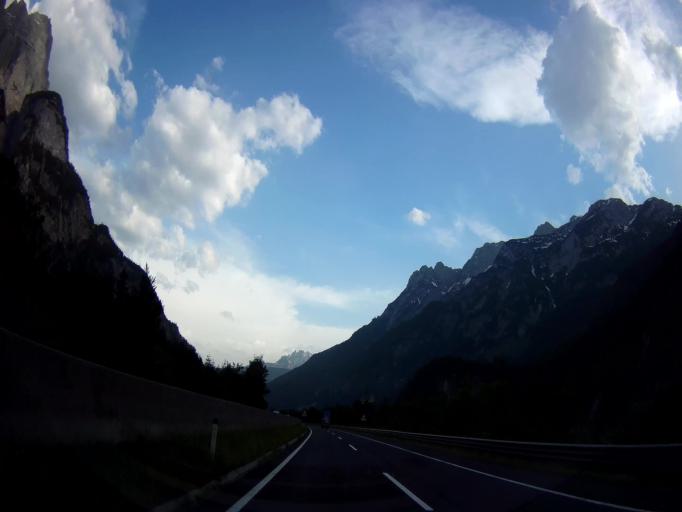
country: AT
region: Salzburg
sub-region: Politischer Bezirk Hallein
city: Golling an der Salzach
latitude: 47.5337
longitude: 13.1714
